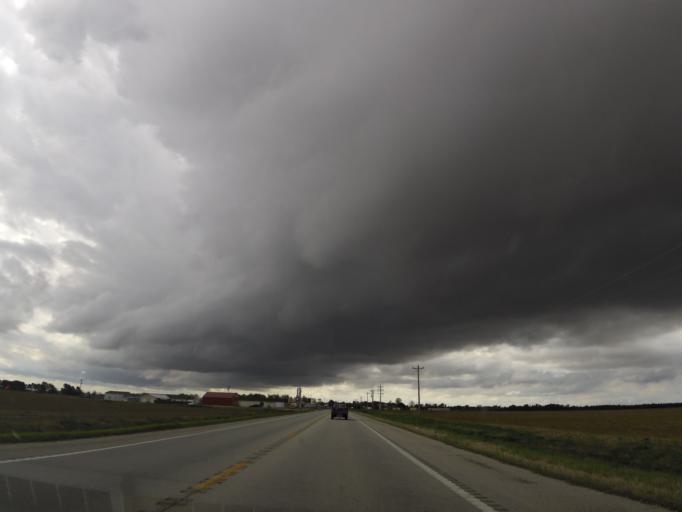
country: US
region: Arkansas
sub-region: Clay County
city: Corning
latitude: 36.5050
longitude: -90.5398
